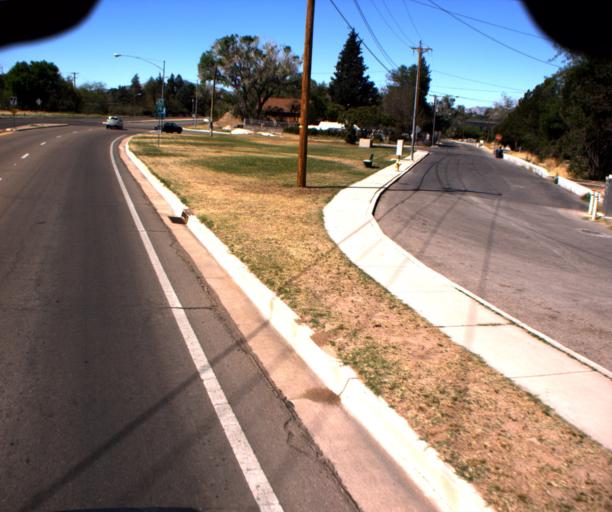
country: US
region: Arizona
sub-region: Santa Cruz County
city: Nogales
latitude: 31.3501
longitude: -110.9238
